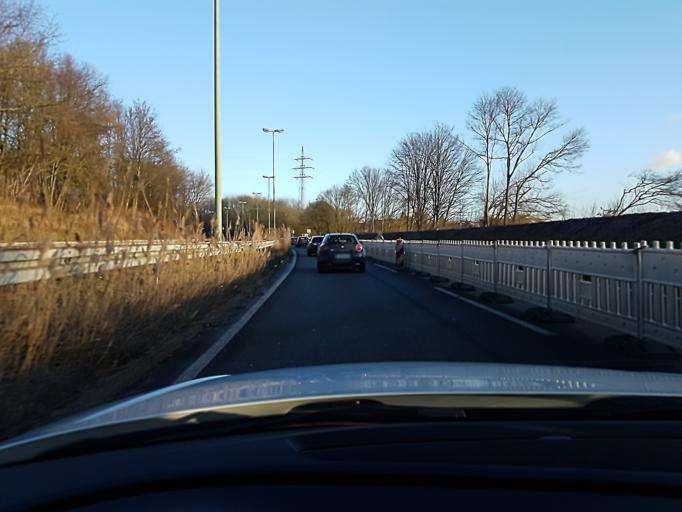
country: DE
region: North Rhine-Westphalia
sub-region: Regierungsbezirk Dusseldorf
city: Essen
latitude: 51.4226
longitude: 7.0656
